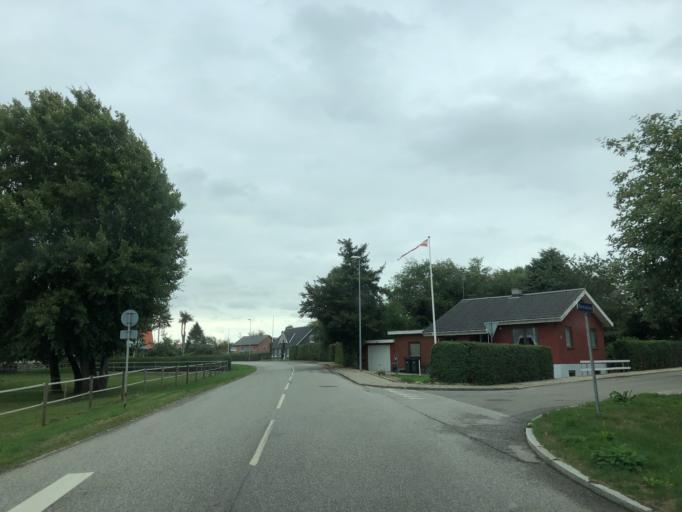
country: DK
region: Central Jutland
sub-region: Herning Kommune
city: Snejbjerg
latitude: 56.1725
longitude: 8.8454
